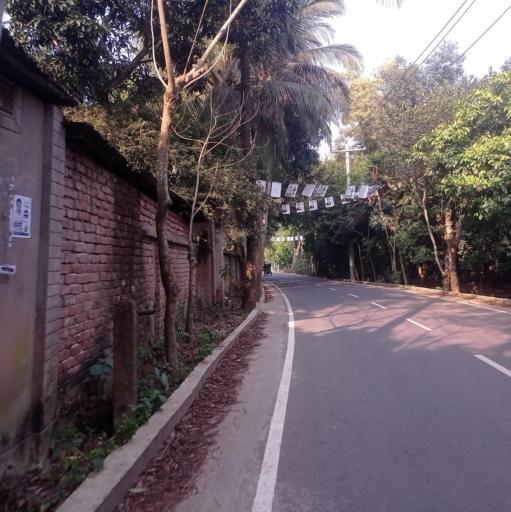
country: BD
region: Dhaka
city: Bhairab Bazar
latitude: 24.0482
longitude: 90.8352
